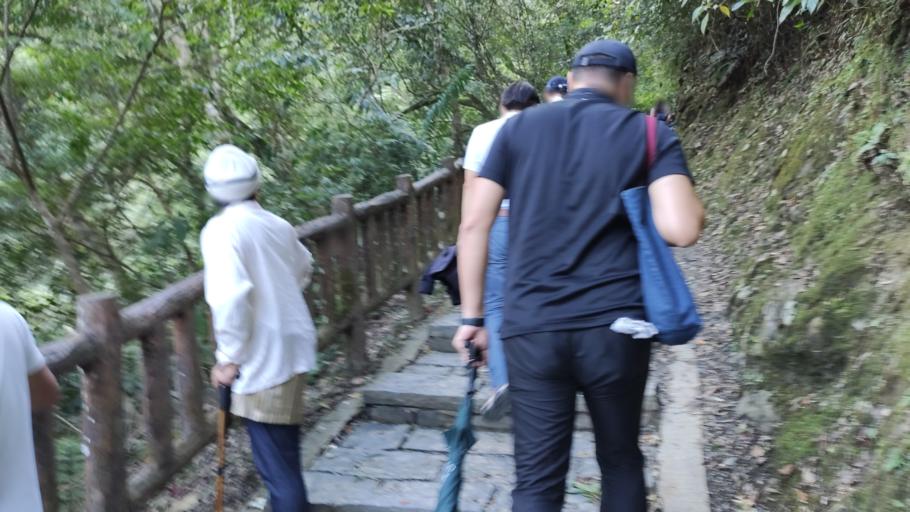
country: TW
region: Taiwan
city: Daxi
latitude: 24.8194
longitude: 121.4499
